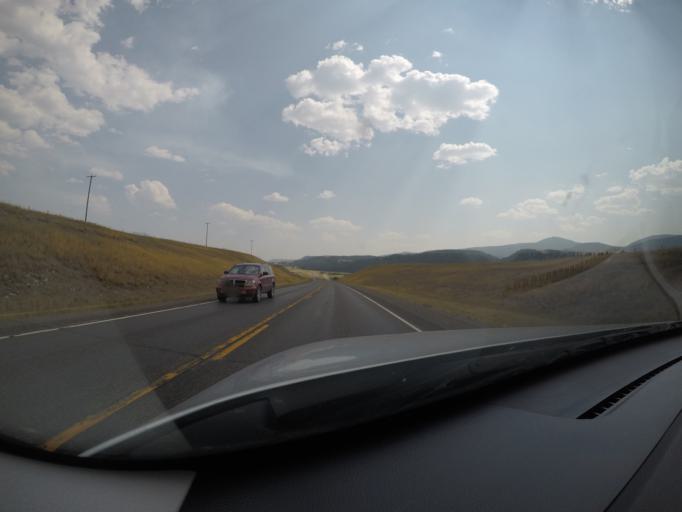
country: US
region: Montana
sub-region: Gallatin County
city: Big Sky
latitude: 44.9819
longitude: -111.6478
